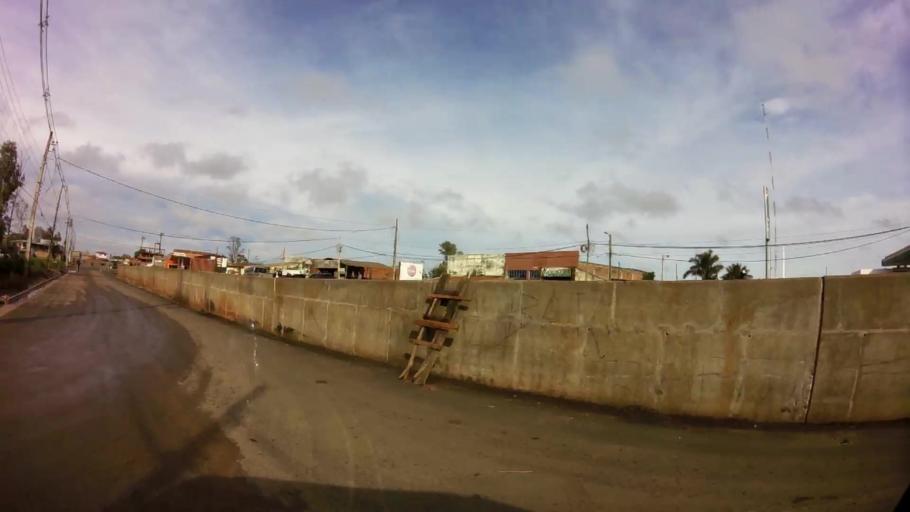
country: PY
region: Central
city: Limpio
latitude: -25.1814
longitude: -57.4907
